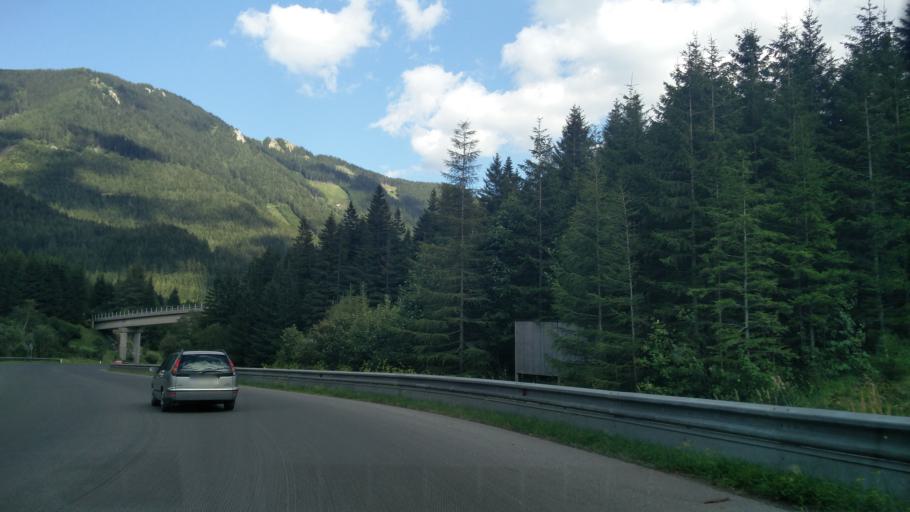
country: AT
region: Styria
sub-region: Politischer Bezirk Leoben
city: Vordernberg
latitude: 47.5163
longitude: 14.9635
